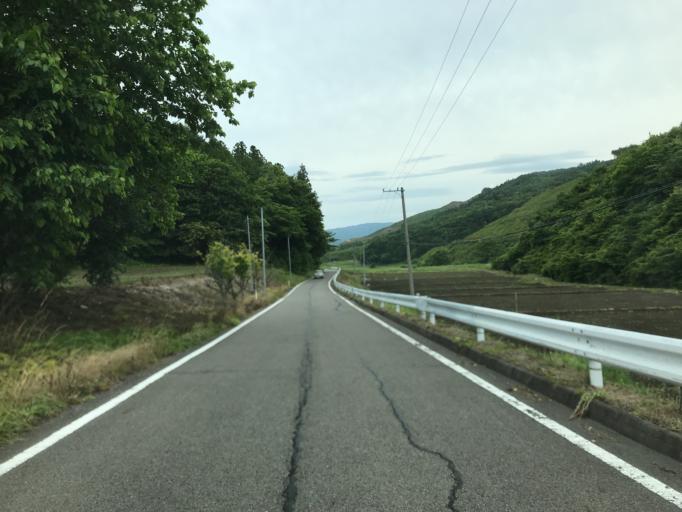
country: JP
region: Fukushima
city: Funehikimachi-funehiki
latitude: 37.4289
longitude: 140.7453
